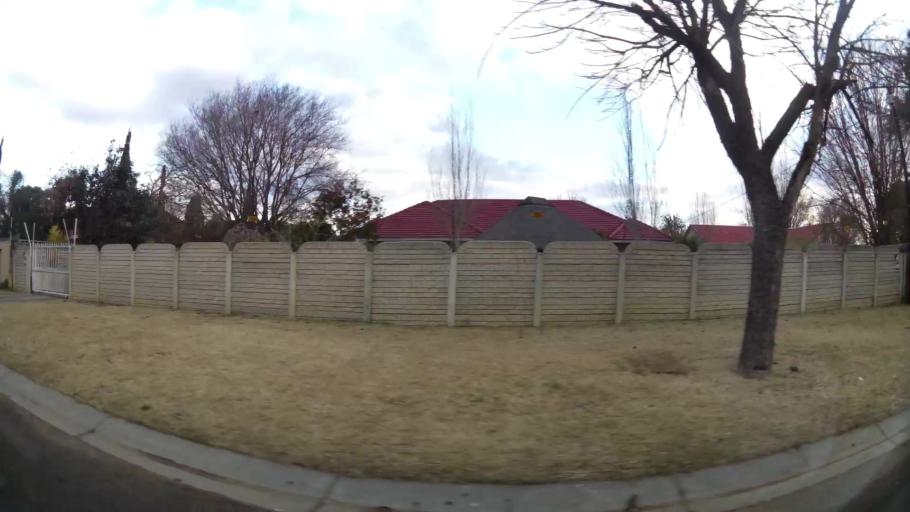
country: ZA
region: Orange Free State
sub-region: Lejweleputswa District Municipality
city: Welkom
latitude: -27.9784
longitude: 26.7237
